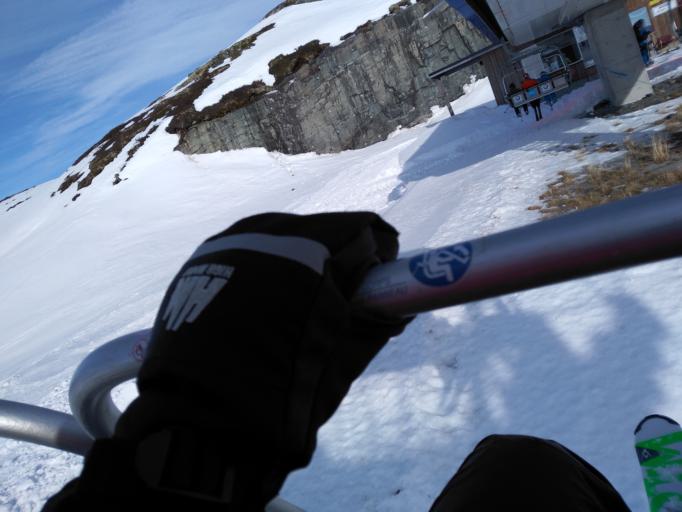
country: NO
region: Aust-Agder
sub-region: Bykle
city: Hovden
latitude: 59.5783
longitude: 7.3217
